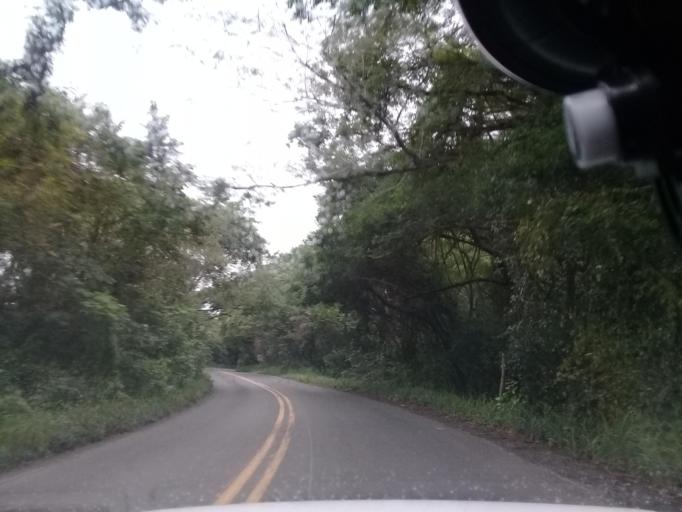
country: MX
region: Veracruz
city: Platon Sanchez
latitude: 21.2397
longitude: -98.3676
